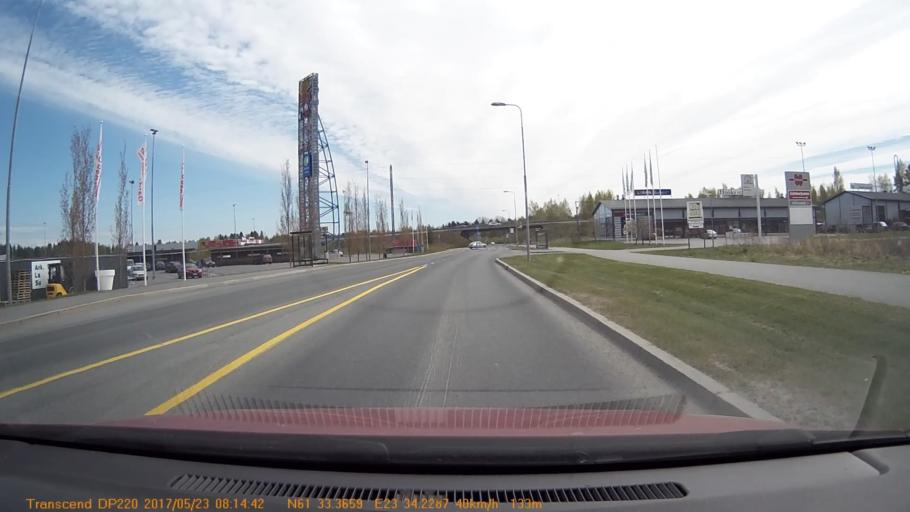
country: FI
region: Pirkanmaa
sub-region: Tampere
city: Yloejaervi
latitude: 61.5561
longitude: 23.5698
